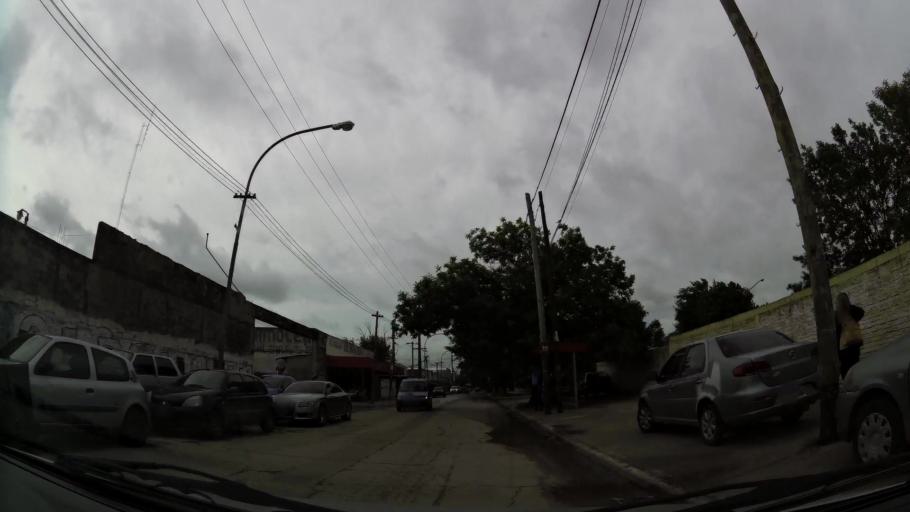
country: AR
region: Buenos Aires
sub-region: Partido de Lanus
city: Lanus
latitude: -34.7346
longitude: -58.3773
